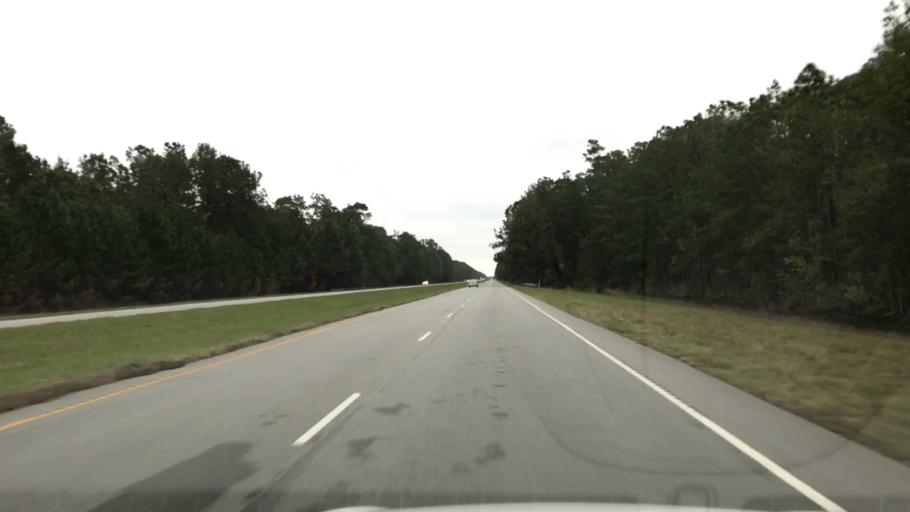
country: US
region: South Carolina
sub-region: Charleston County
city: Awendaw
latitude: 33.1381
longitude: -79.4414
